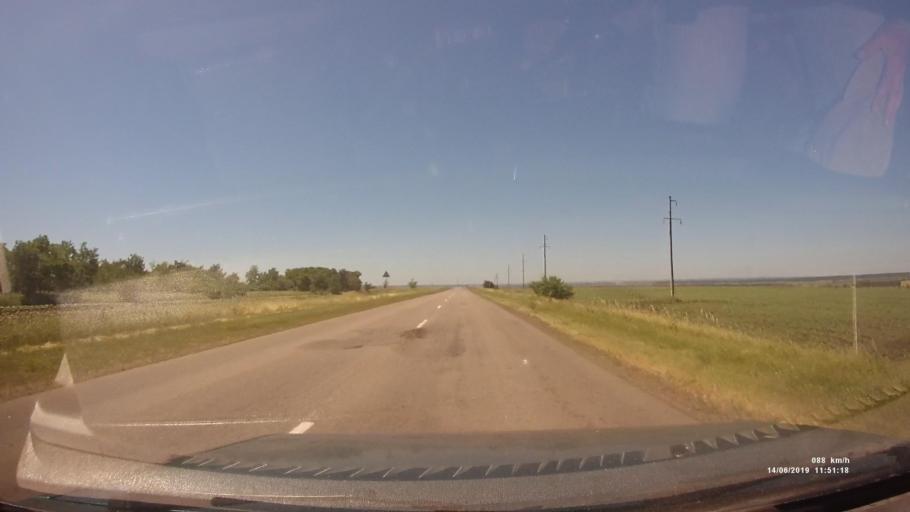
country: RU
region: Rostov
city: Kazanskaya
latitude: 49.8431
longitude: 41.2489
